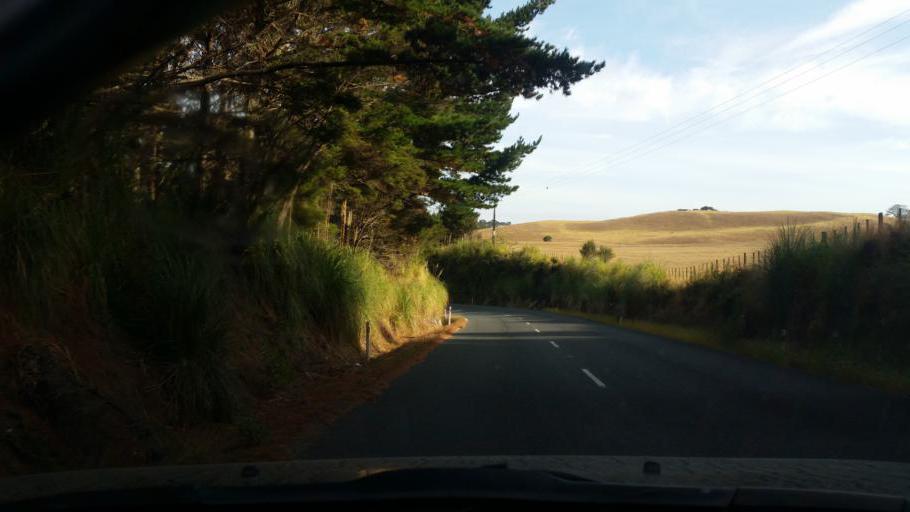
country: NZ
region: Northland
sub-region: Kaipara District
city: Dargaville
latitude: -36.2316
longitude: 174.0450
